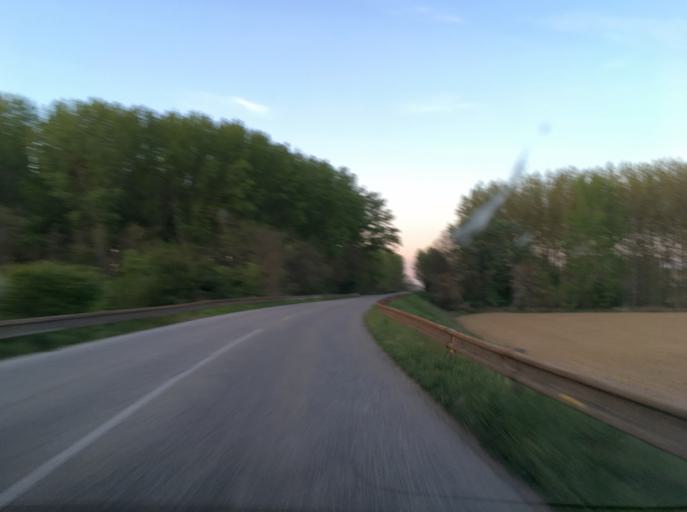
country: SK
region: Nitriansky
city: Kolarovo
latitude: 47.9193
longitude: 18.0113
